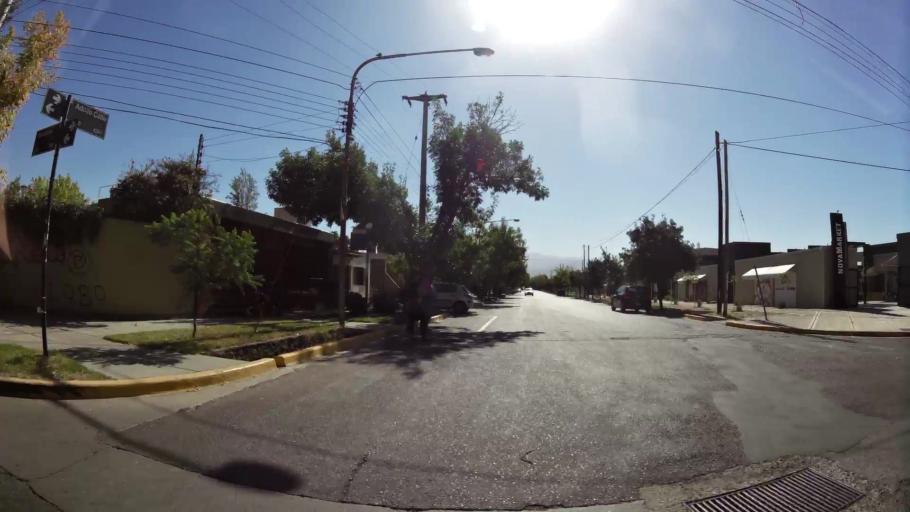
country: AR
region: Mendoza
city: Villa Nueva
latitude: -32.9088
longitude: -68.7908
